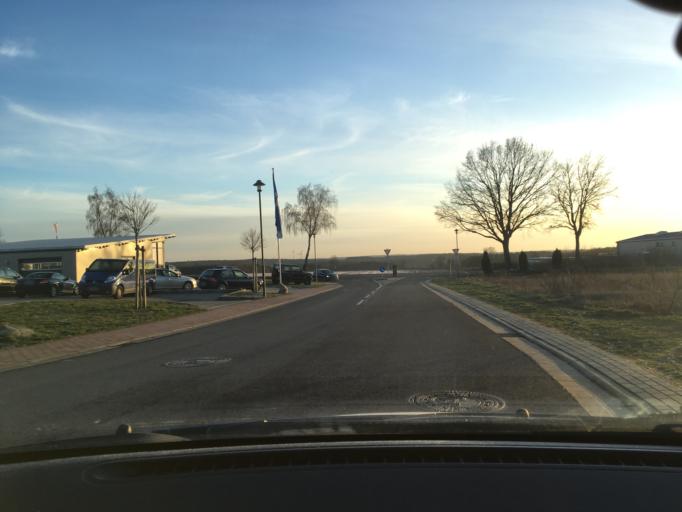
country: DE
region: Lower Saxony
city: Egestorf
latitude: 53.1949
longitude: 10.0740
